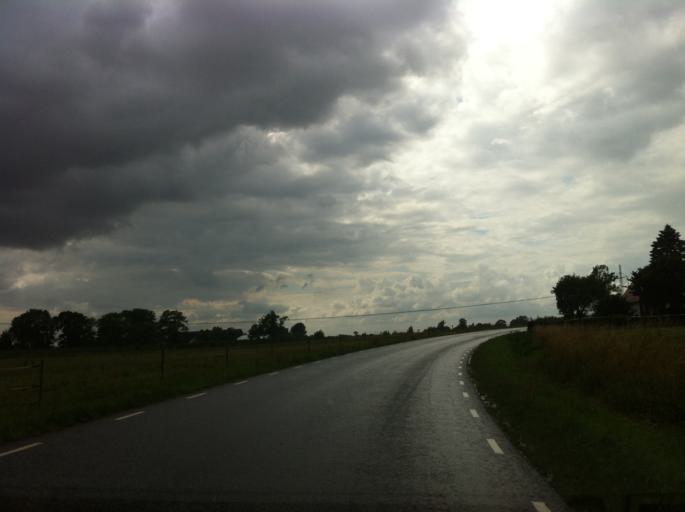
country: SE
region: Skane
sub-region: Lunds Kommun
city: Lund
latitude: 55.7943
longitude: 13.2082
